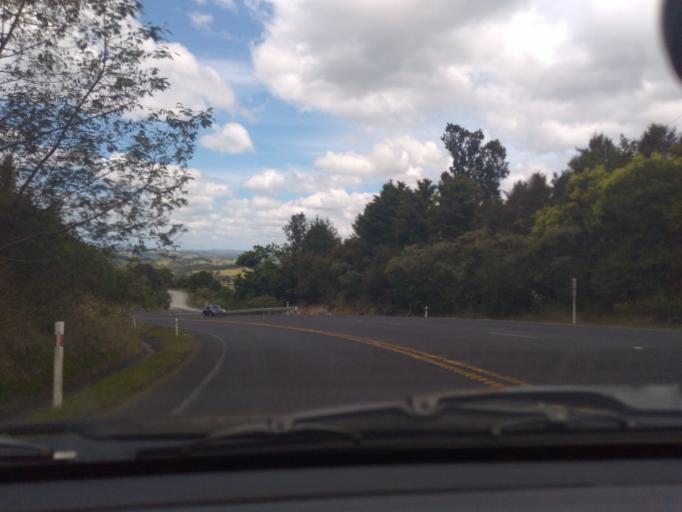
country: NZ
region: Northland
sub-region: Far North District
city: Moerewa
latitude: -35.3895
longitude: 173.9957
